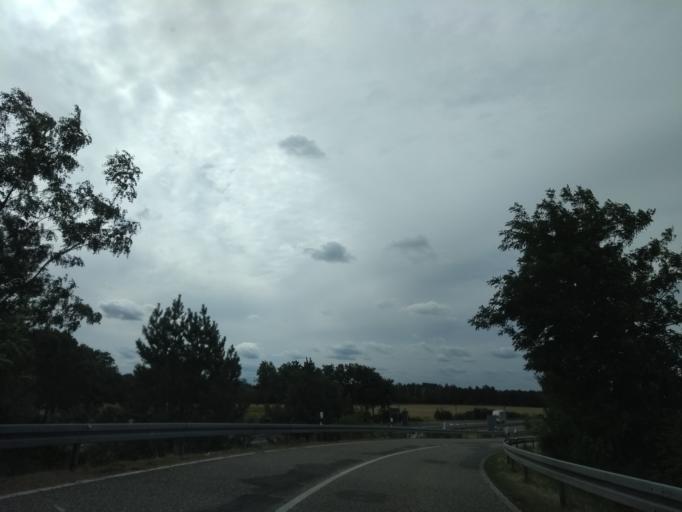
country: DE
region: Brandenburg
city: Lubbenau
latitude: 51.8309
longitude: 13.9109
